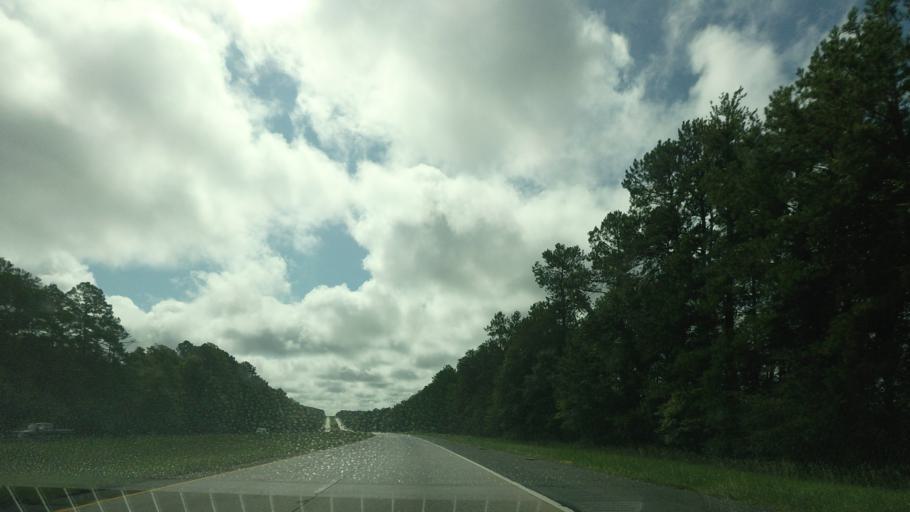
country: US
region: Georgia
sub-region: Houston County
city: Robins Air Force Base
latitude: 32.6780
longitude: -83.4829
